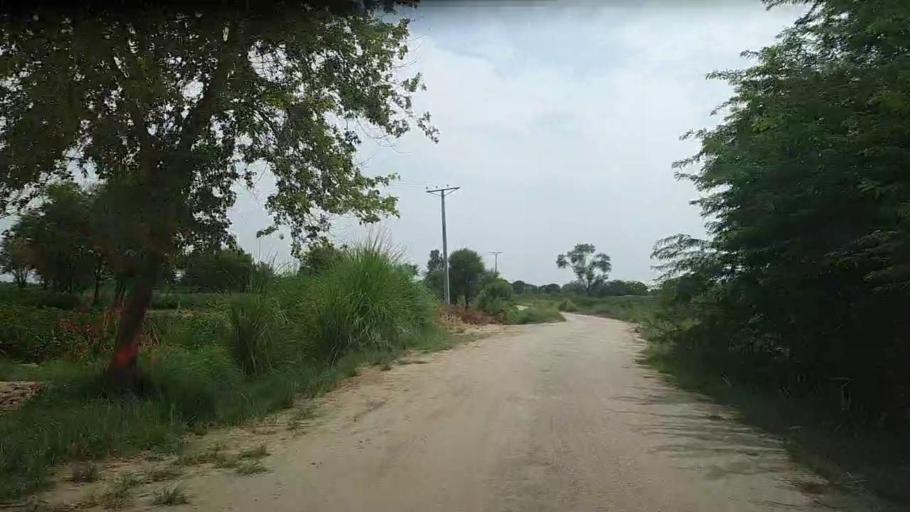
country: PK
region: Sindh
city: Bhiria
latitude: 26.8828
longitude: 68.2954
